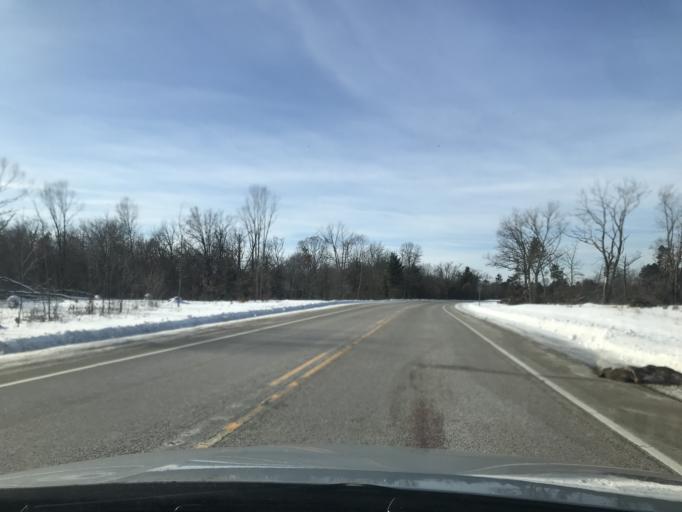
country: US
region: Wisconsin
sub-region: Oconto County
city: Gillett
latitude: 45.1148
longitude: -88.3737
